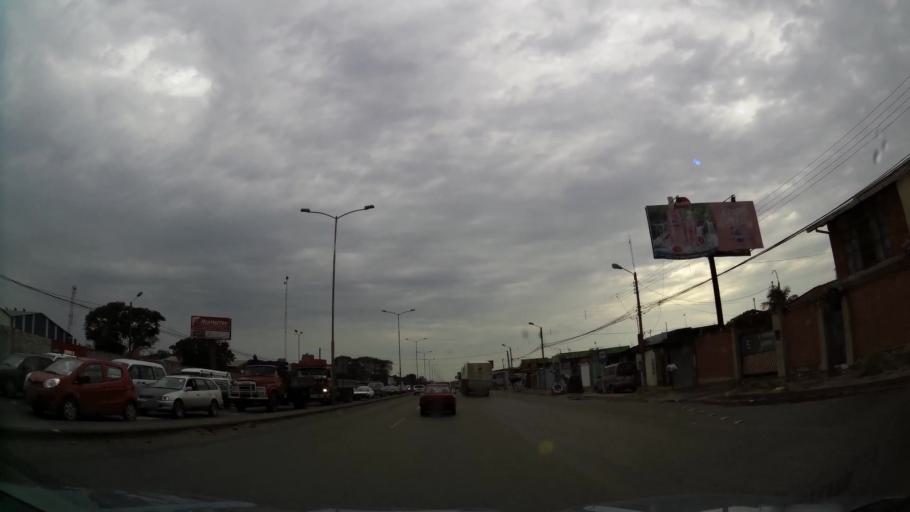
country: BO
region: Santa Cruz
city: Santa Cruz de la Sierra
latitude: -17.7774
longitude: -63.1410
